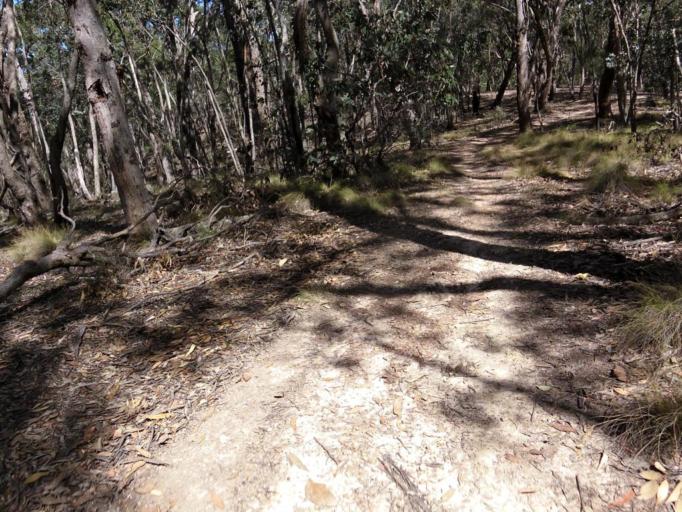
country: AU
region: Victoria
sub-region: Melton
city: Melton West
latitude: -37.4875
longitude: 144.5374
